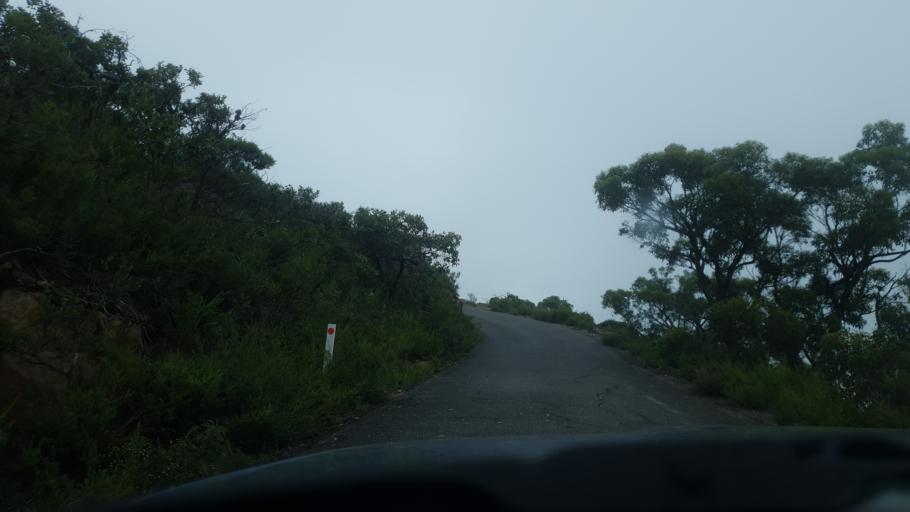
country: AU
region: Victoria
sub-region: Northern Grampians
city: Stawell
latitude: -37.2722
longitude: 142.5815
